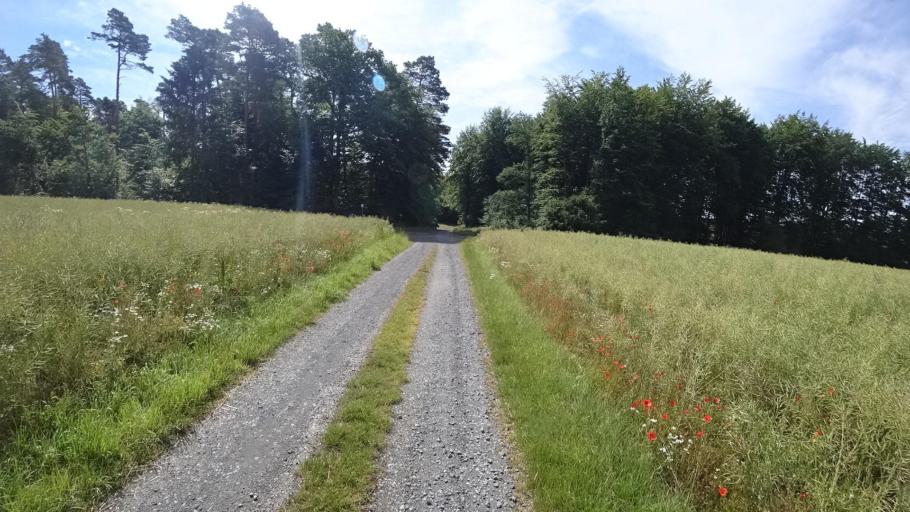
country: DE
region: Rheinland-Pfalz
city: Schoneberg
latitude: 50.6567
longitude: 7.5878
